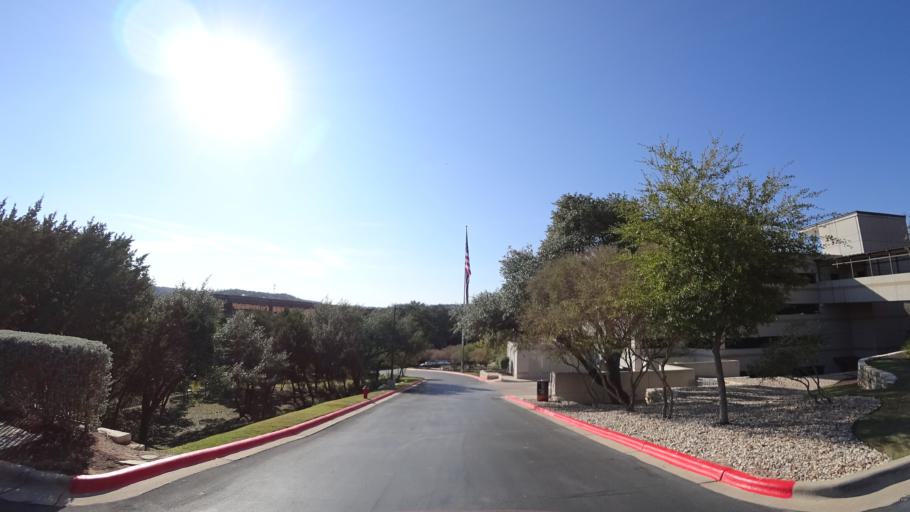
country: US
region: Texas
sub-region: Williamson County
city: Jollyville
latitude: 30.3871
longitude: -97.7684
